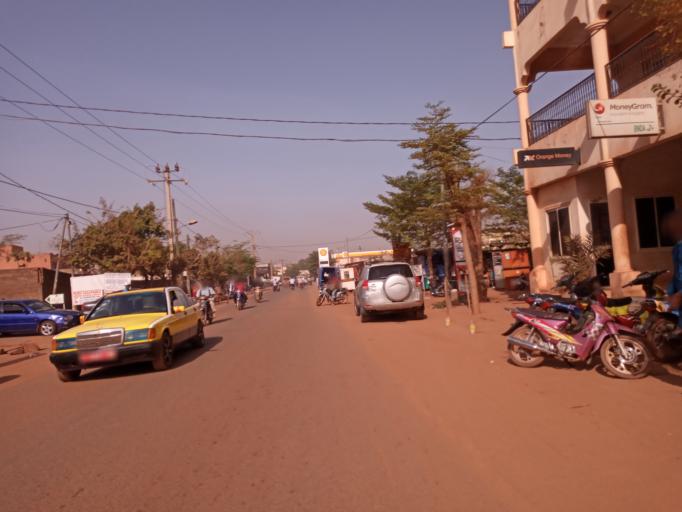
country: ML
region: Bamako
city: Bamako
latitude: 12.5884
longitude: -7.9762
